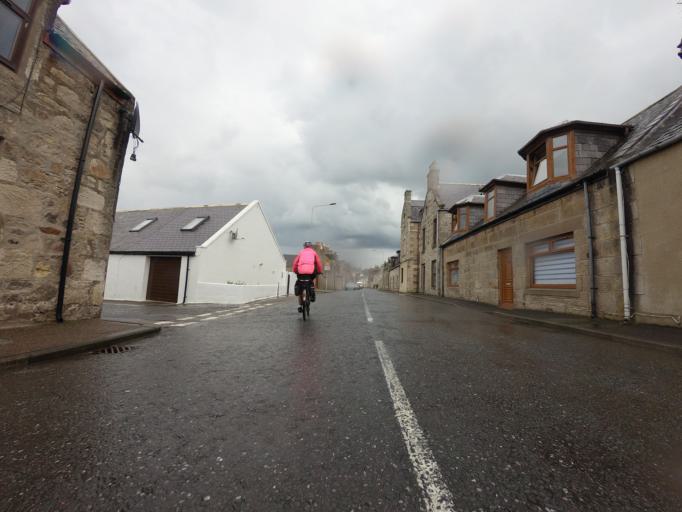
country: GB
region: Scotland
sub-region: Moray
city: Buckie
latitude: 57.6757
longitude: -2.9788
